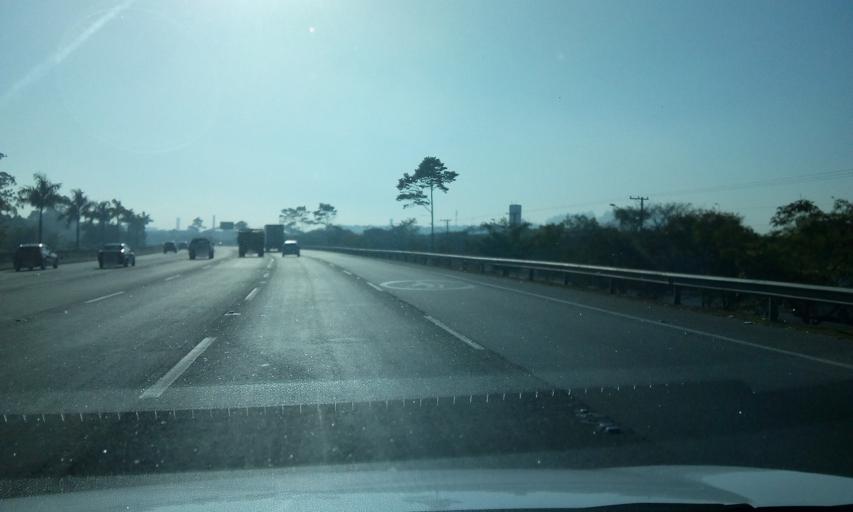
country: BR
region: Sao Paulo
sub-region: Guarulhos
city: Guarulhos
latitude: -23.4919
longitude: -46.5116
